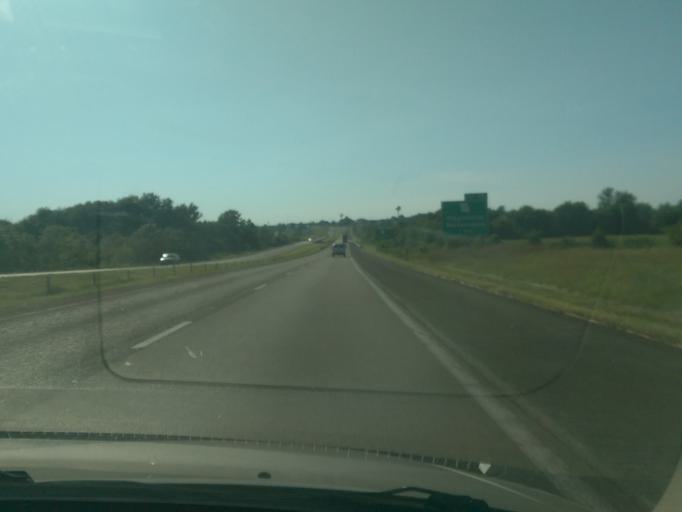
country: US
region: Missouri
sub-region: Lafayette County
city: Higginsville
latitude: 38.9945
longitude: -93.7134
